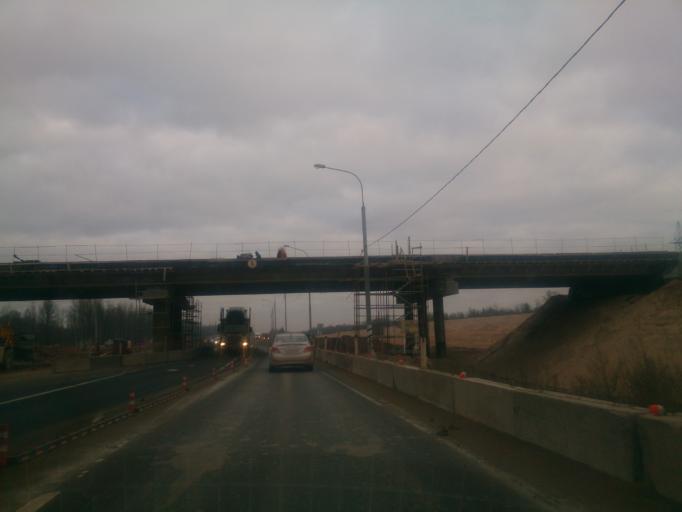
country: RU
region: Novgorod
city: Krechevitsy
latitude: 58.8050
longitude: 31.4637
